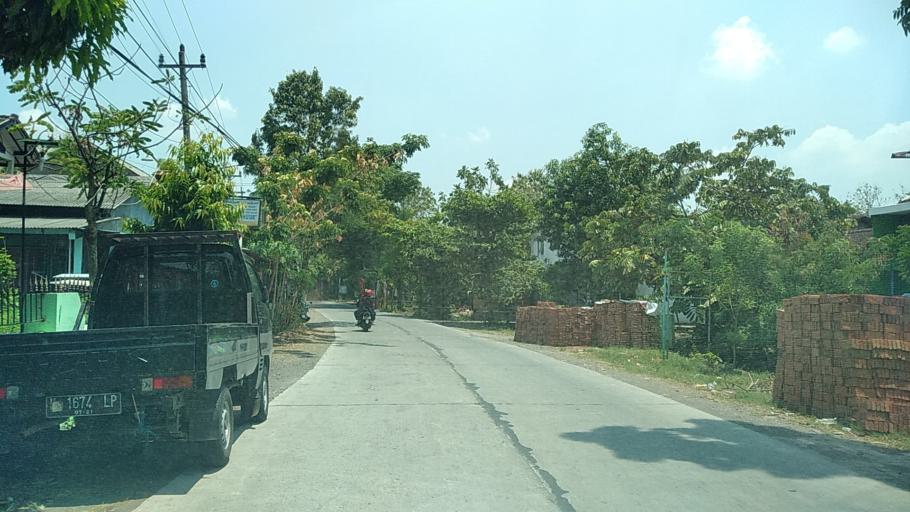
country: ID
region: Central Java
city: Mranggen
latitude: -7.0145
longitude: 110.4861
